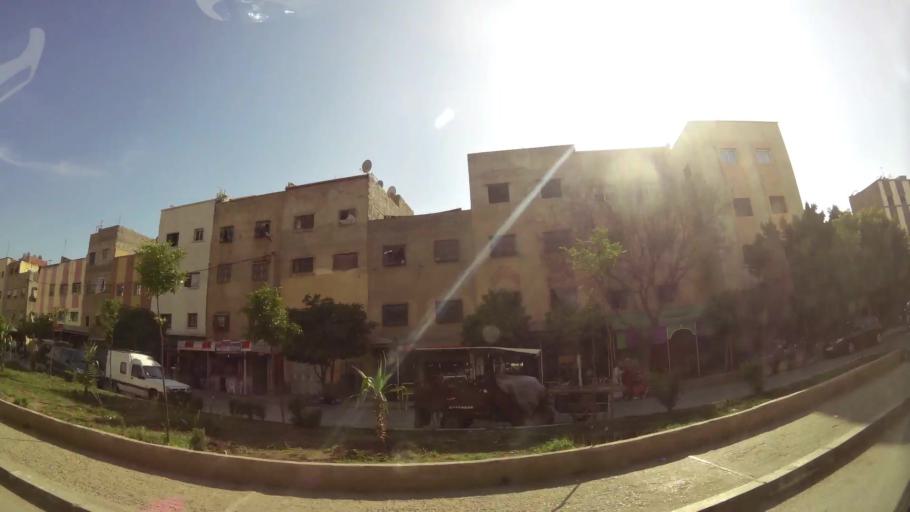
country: MA
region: Fes-Boulemane
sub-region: Fes
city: Fes
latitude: 34.0186
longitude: -5.0338
